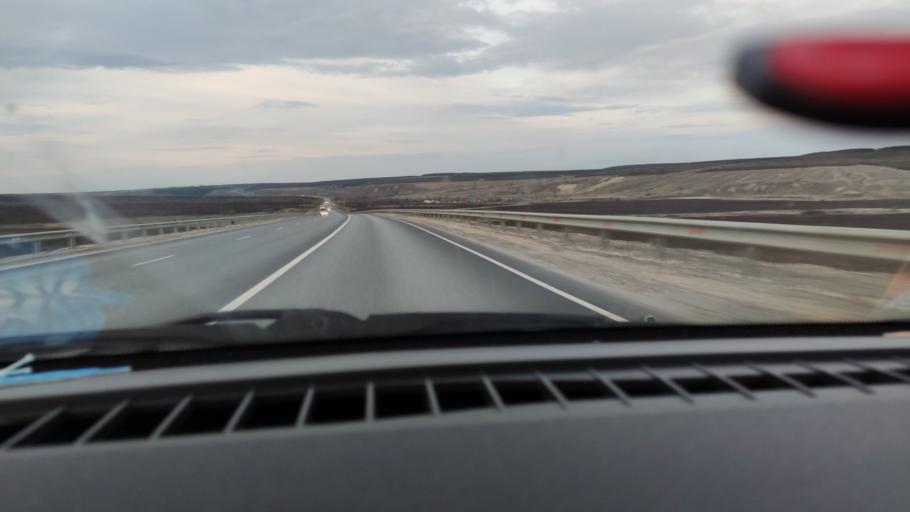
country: RU
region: Saratov
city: Yelshanka
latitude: 51.8426
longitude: 46.4801
